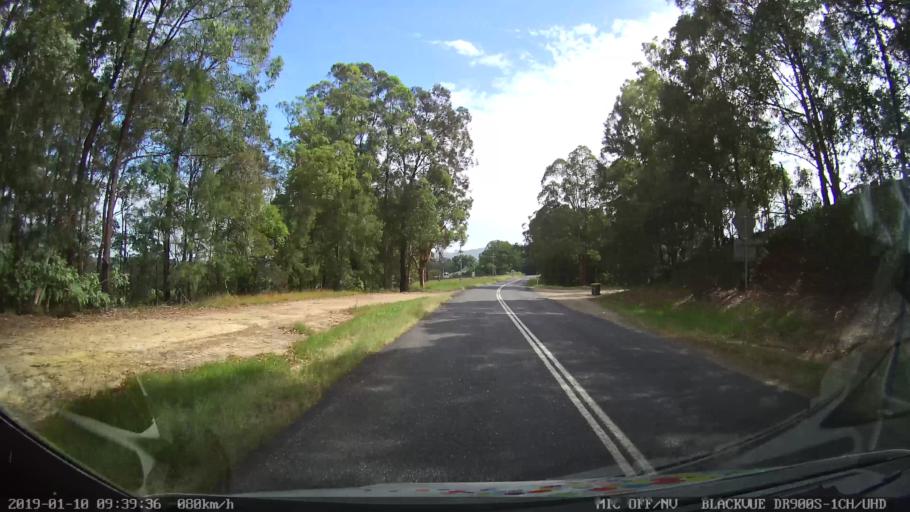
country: AU
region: New South Wales
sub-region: Coffs Harbour
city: Nana Glen
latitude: -30.1615
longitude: 153.0031
